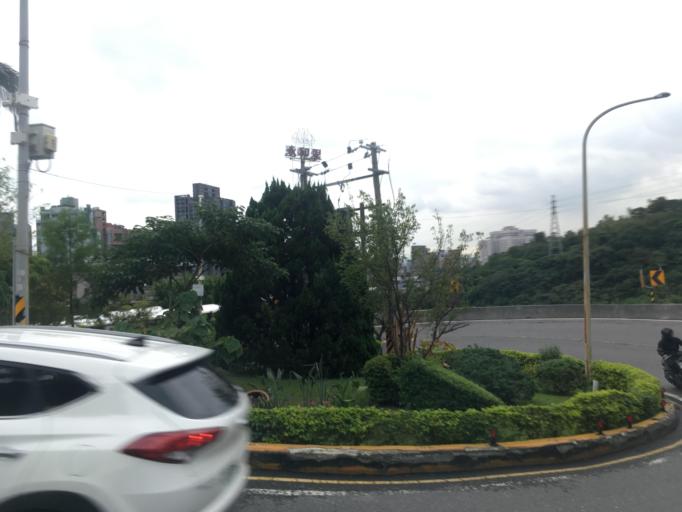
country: TW
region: Taipei
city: Taipei
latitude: 25.1281
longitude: 121.5280
